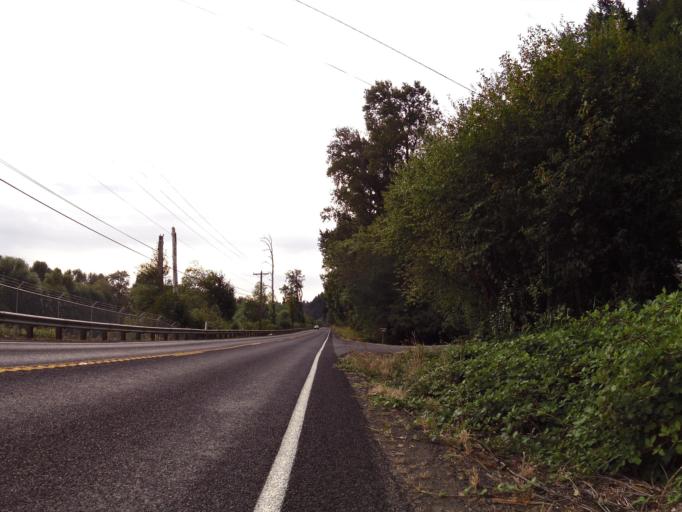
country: US
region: Washington
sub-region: Cowlitz County
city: West Longview
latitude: 46.1885
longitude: -123.1013
